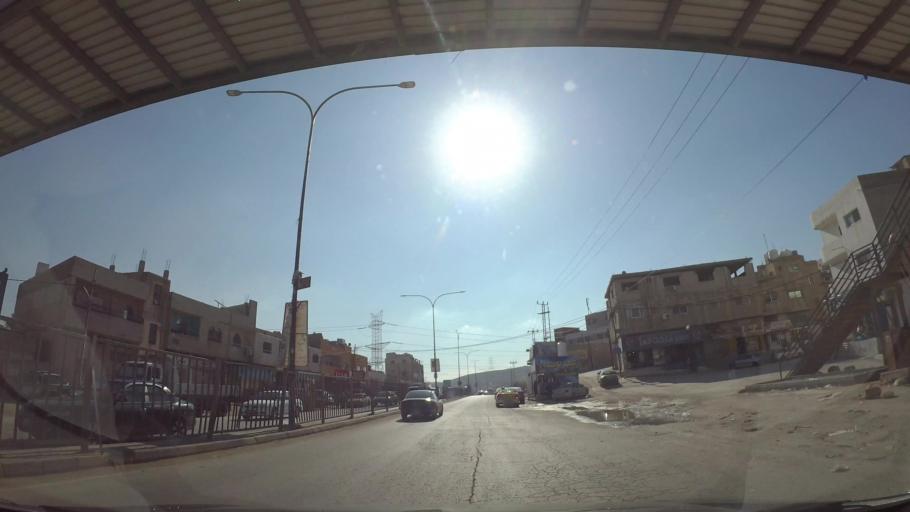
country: JO
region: Zarqa
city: Russeifa
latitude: 32.0201
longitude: 36.0076
